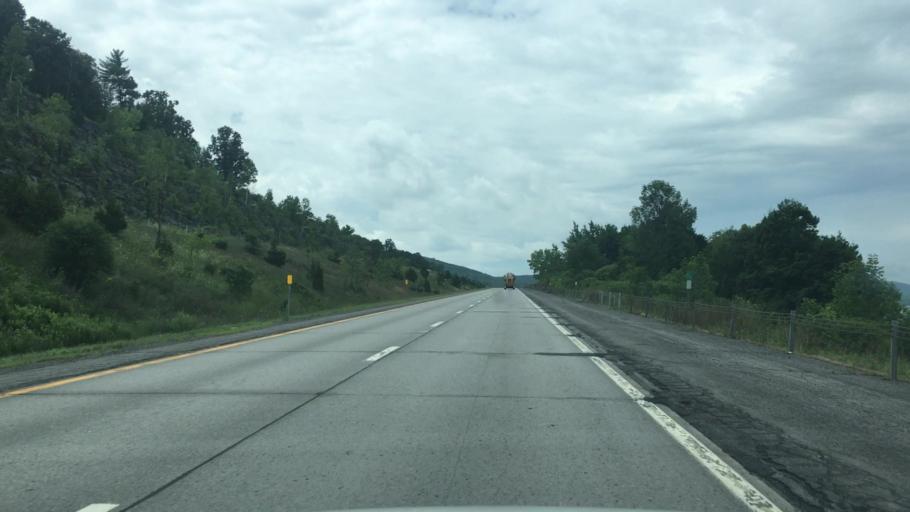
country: US
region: New York
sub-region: Schoharie County
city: Schoharie
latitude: 42.6954
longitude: -74.3490
